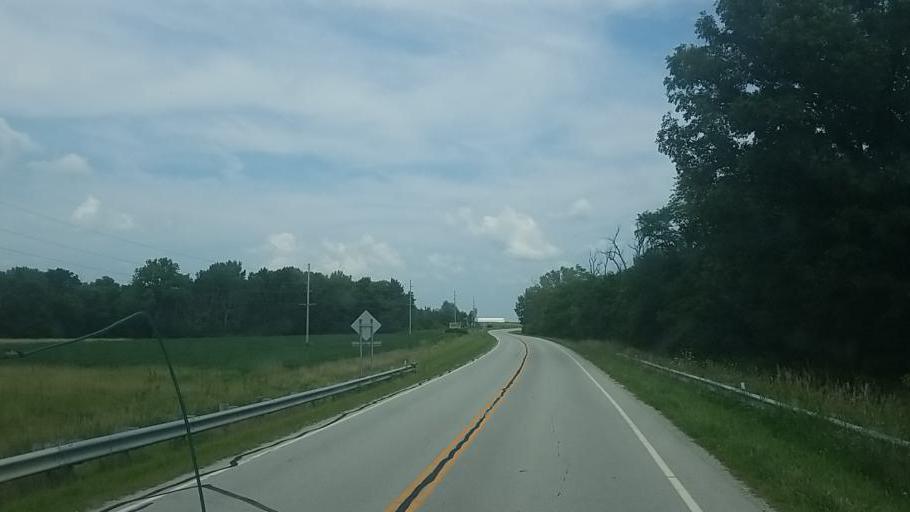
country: US
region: Ohio
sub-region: Hardin County
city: Forest
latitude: 40.7821
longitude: -83.5743
